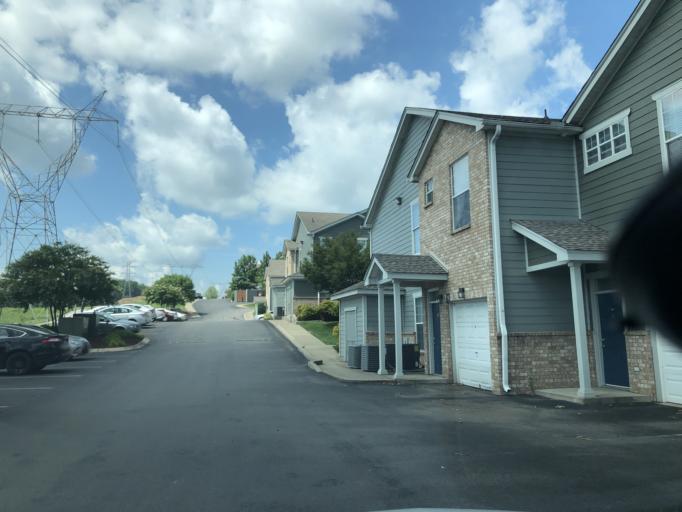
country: US
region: Tennessee
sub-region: Rutherford County
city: La Vergne
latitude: 36.0439
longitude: -86.6110
